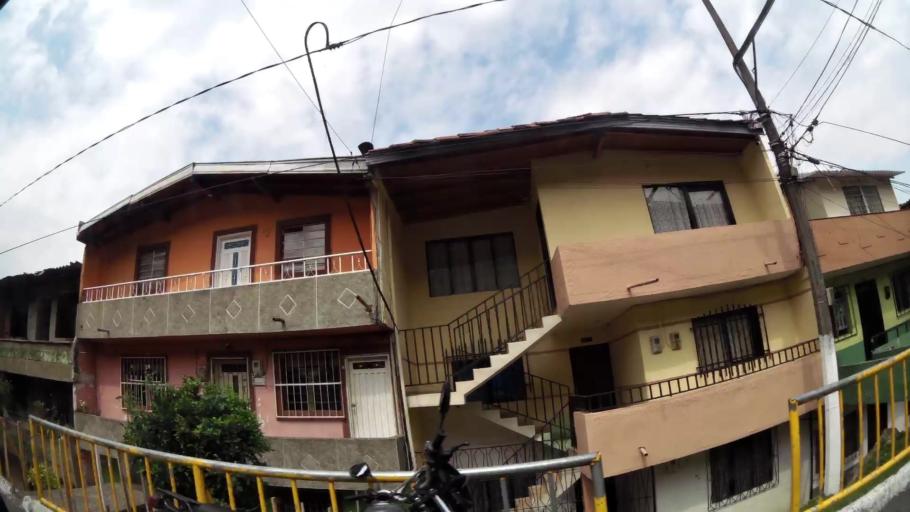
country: CO
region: Antioquia
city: Medellin
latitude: 6.2760
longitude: -75.5504
